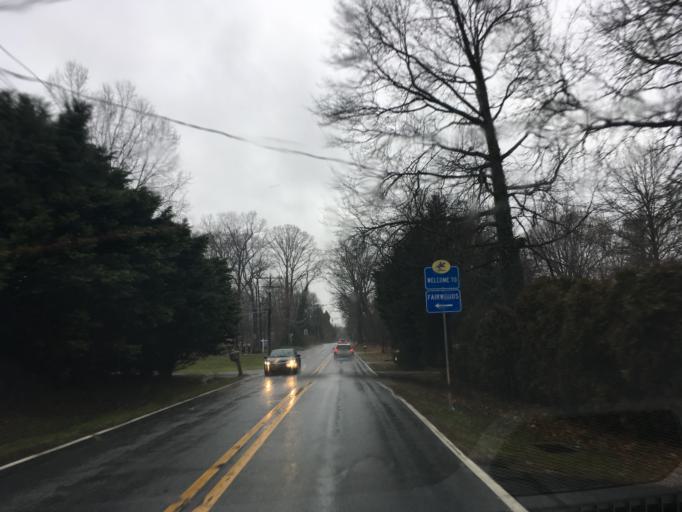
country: US
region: Delaware
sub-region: New Castle County
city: Bellefonte
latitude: 39.8186
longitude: -75.5128
